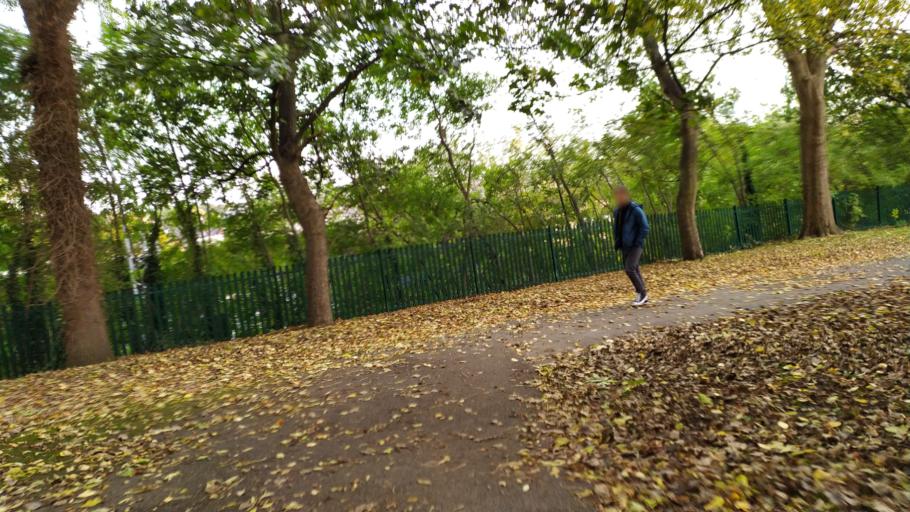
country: GB
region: England
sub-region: City and Borough of Leeds
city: Leeds
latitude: 53.8093
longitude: -1.5765
